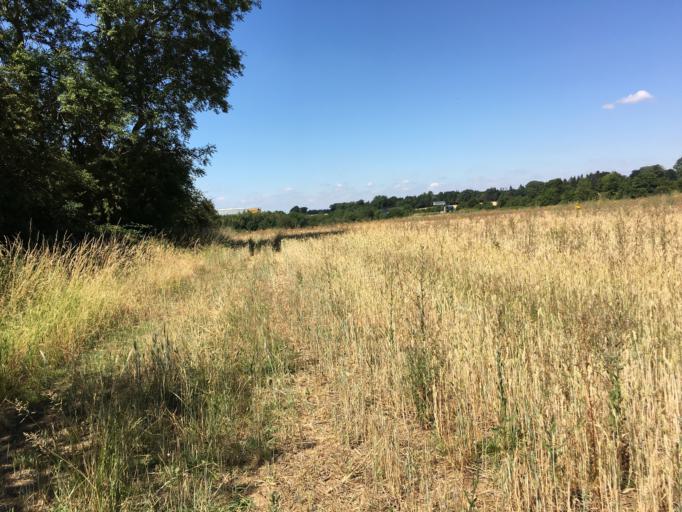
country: GB
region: England
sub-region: Warwickshire
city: Rugby
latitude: 52.4048
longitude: -1.2260
